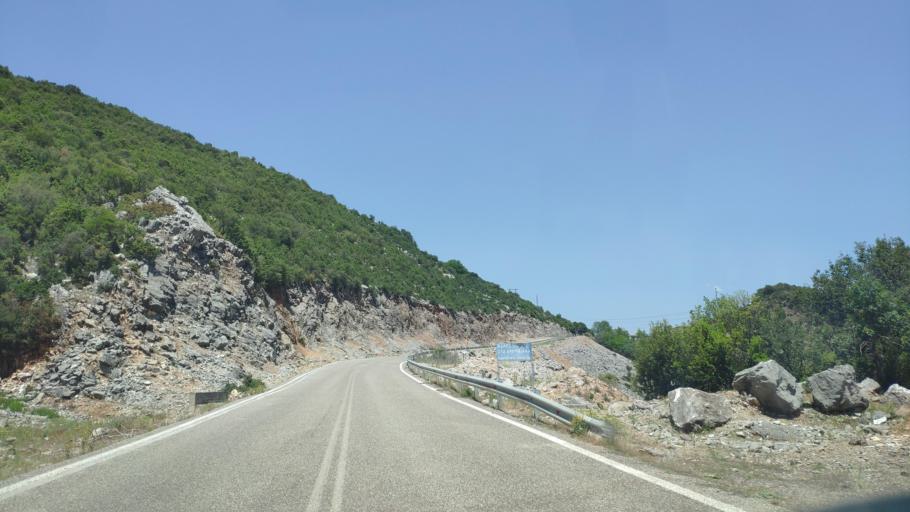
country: GR
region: Central Greece
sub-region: Nomos Evrytanias
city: Kerasochori
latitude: 39.1015
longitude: 21.4109
